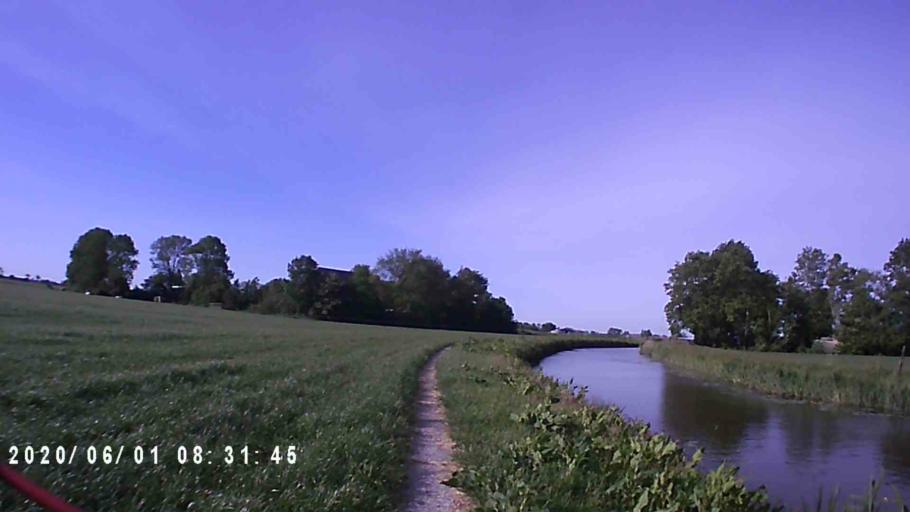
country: NL
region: Friesland
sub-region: Gemeente Ferwerderadiel
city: Burdaard
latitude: 53.2994
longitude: 5.8492
